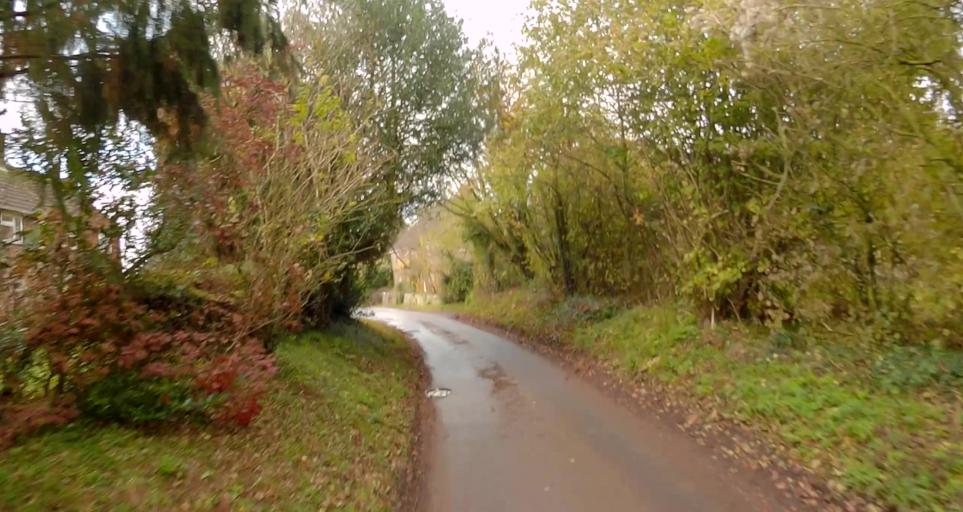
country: GB
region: England
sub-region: Hampshire
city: Long Sutton
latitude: 51.2173
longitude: -0.9440
